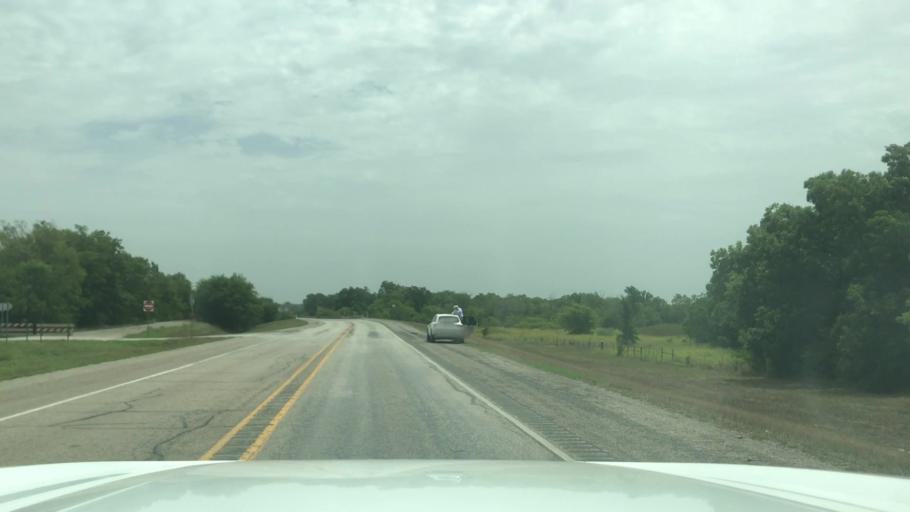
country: US
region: Texas
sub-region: Hamilton County
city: Hico
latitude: 32.0395
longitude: -98.1138
